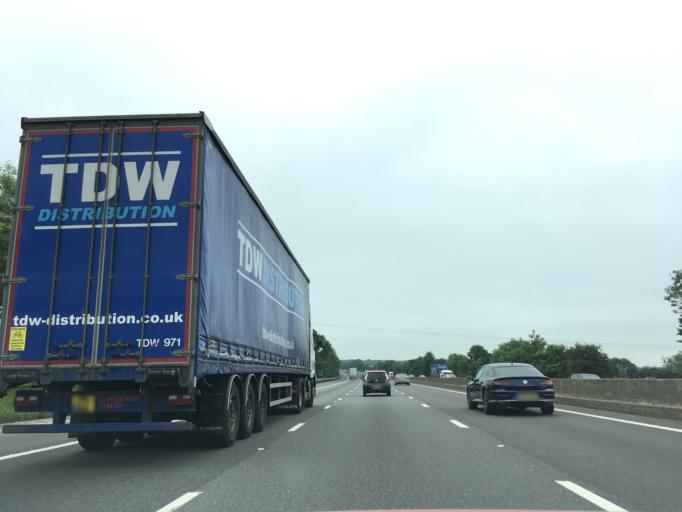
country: GB
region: England
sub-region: West Berkshire
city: Lambourn
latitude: 51.4744
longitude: -1.5390
